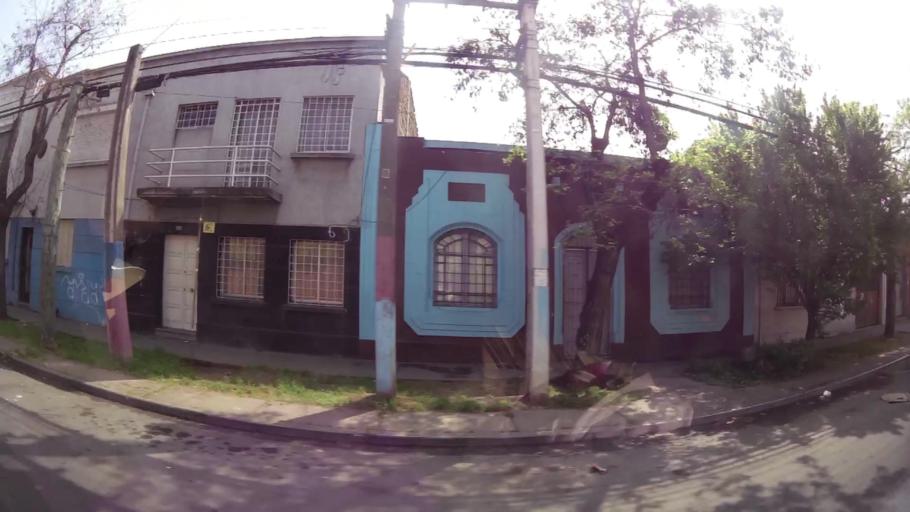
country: CL
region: Santiago Metropolitan
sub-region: Provincia de Santiago
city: Santiago
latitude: -33.4671
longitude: -70.6467
